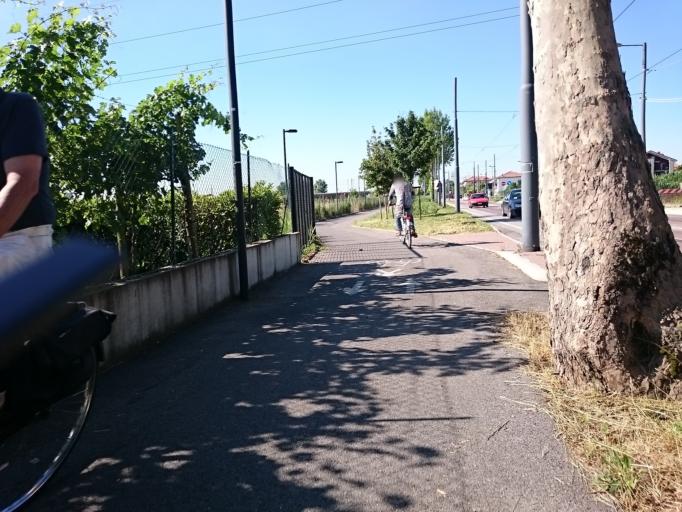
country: IT
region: Veneto
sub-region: Provincia di Padova
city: Mandriola-Sant'Agostino
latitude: 45.3696
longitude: 11.8724
